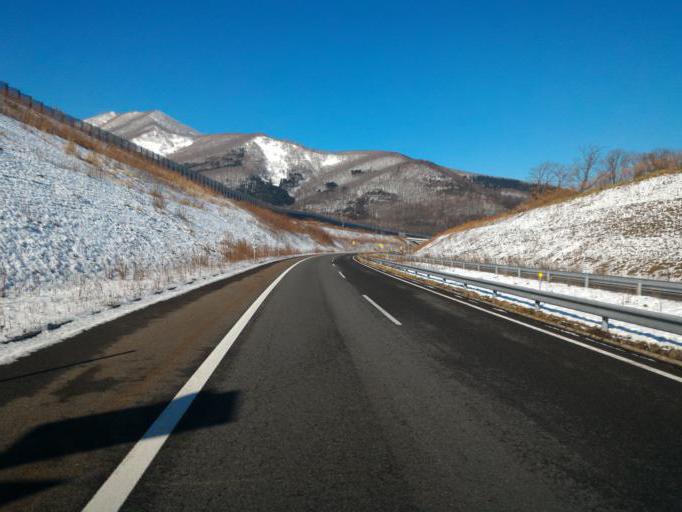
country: JP
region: Hokkaido
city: Otofuke
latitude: 43.0358
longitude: 142.7876
